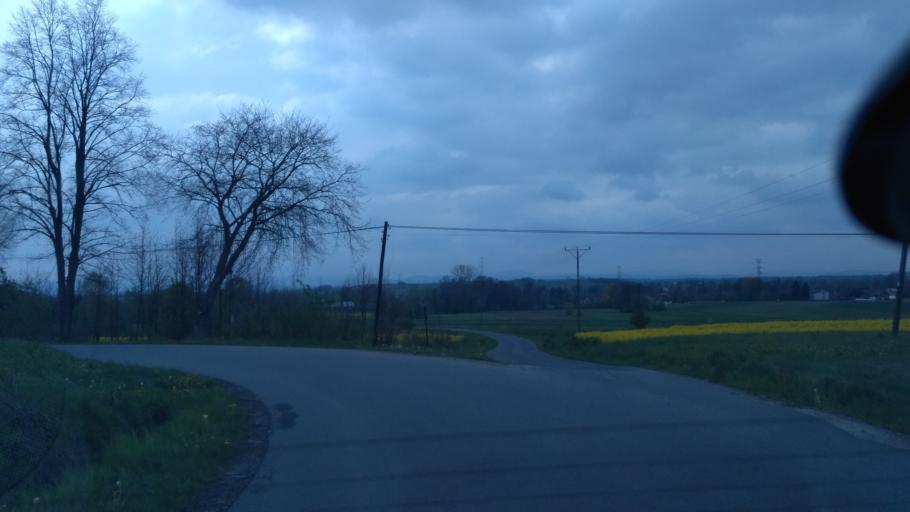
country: PL
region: Subcarpathian Voivodeship
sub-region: Powiat brzozowski
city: Jablonica Polska
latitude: 49.6895
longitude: 21.8919
